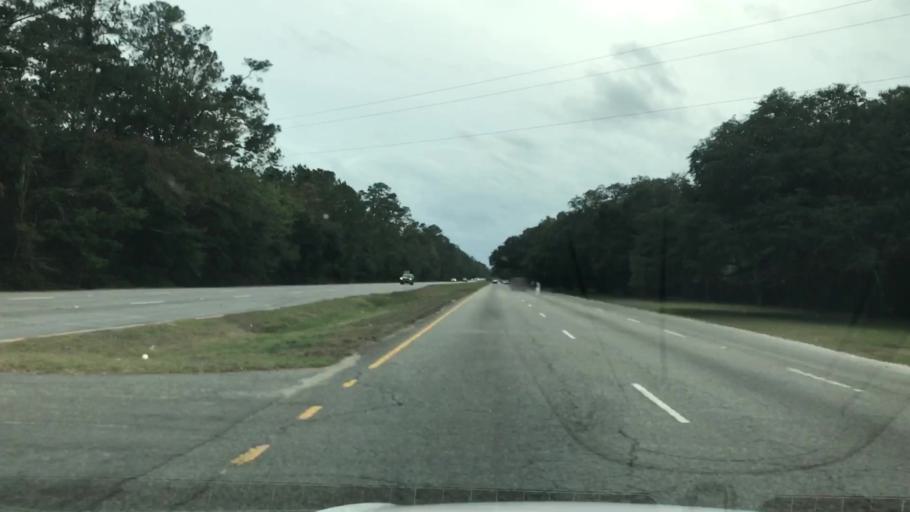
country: US
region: South Carolina
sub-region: Georgetown County
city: Murrells Inlet
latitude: 33.5084
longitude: -79.0774
